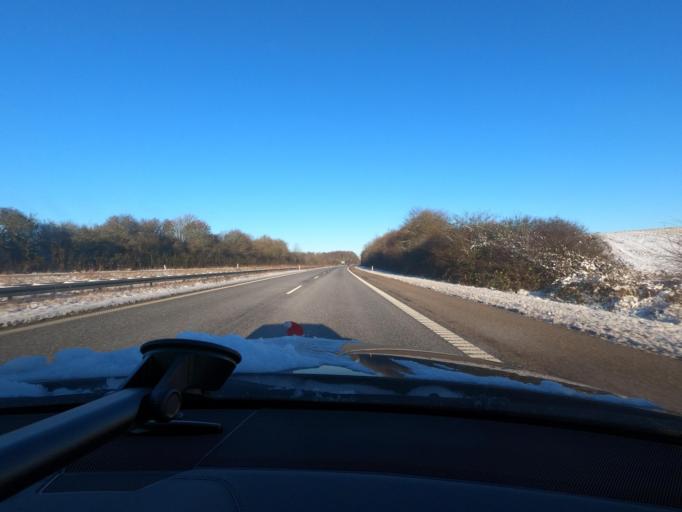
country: DK
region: South Denmark
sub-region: Aabenraa Kommune
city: Rodekro
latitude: 55.0530
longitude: 9.3536
